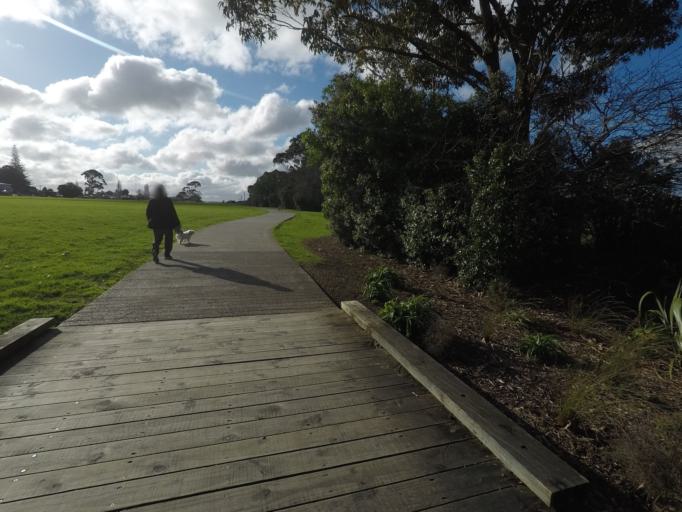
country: NZ
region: Auckland
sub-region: Auckland
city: Rosebank
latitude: -36.8956
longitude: 174.6718
